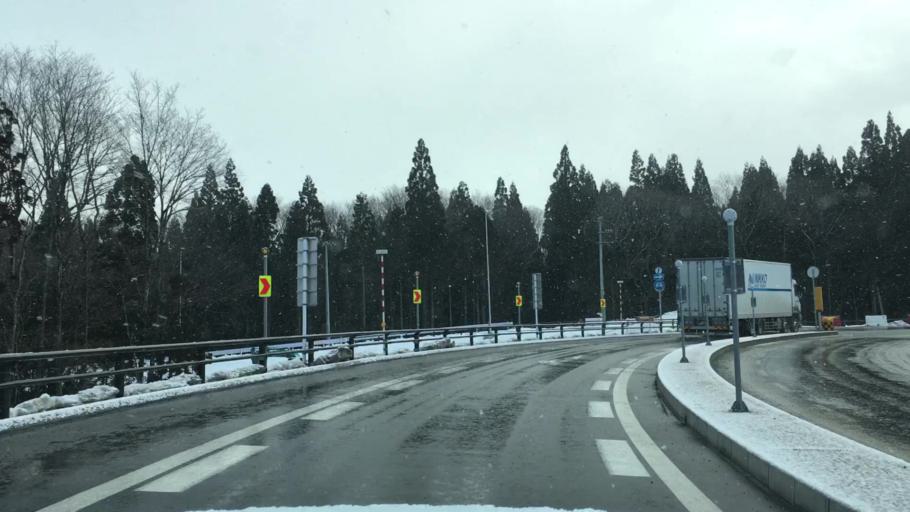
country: JP
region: Akita
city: Takanosu
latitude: 40.2002
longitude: 140.3741
